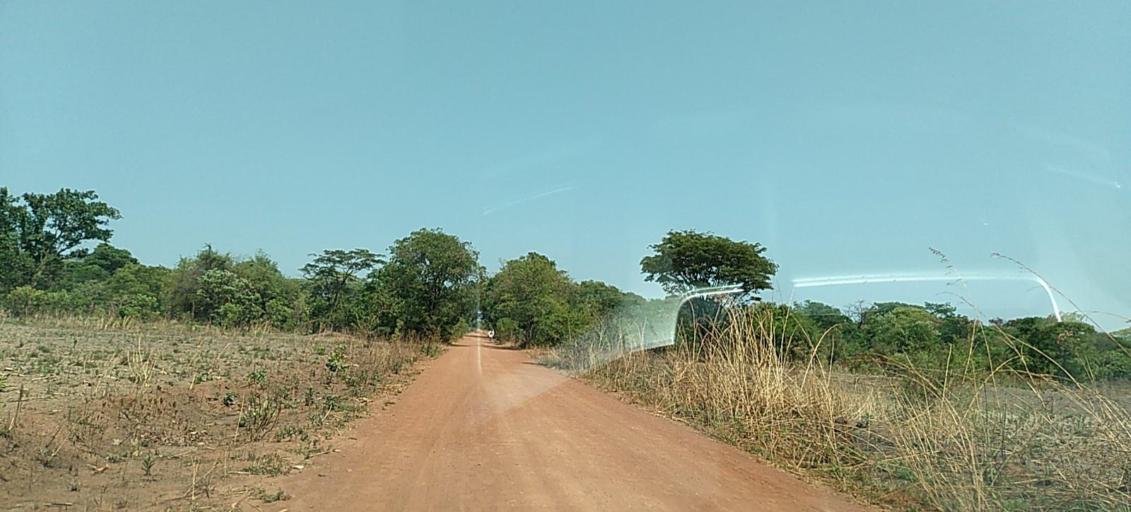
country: ZM
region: Copperbelt
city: Chingola
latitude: -12.5416
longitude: 27.7374
